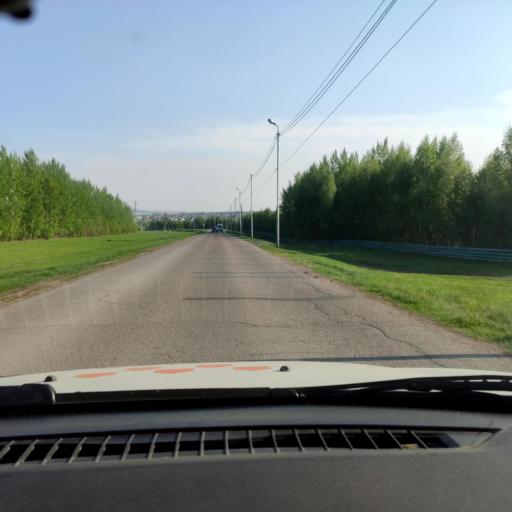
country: RU
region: Bashkortostan
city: Karmaskaly
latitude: 54.3777
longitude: 56.1513
